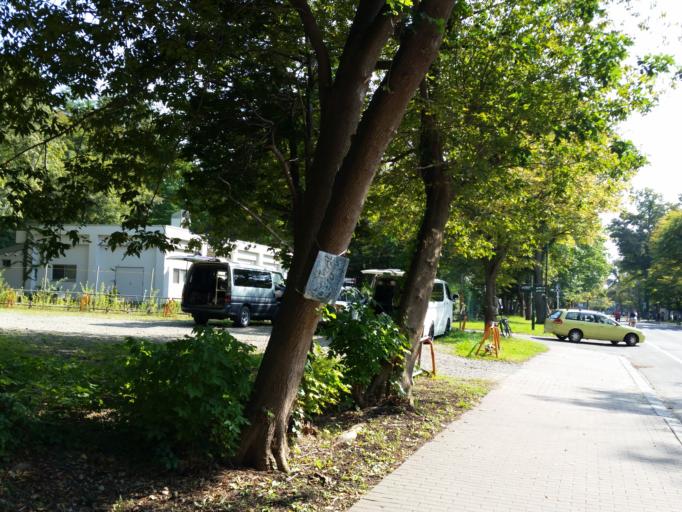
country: JP
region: Hokkaido
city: Sapporo
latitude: 43.0740
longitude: 141.3423
